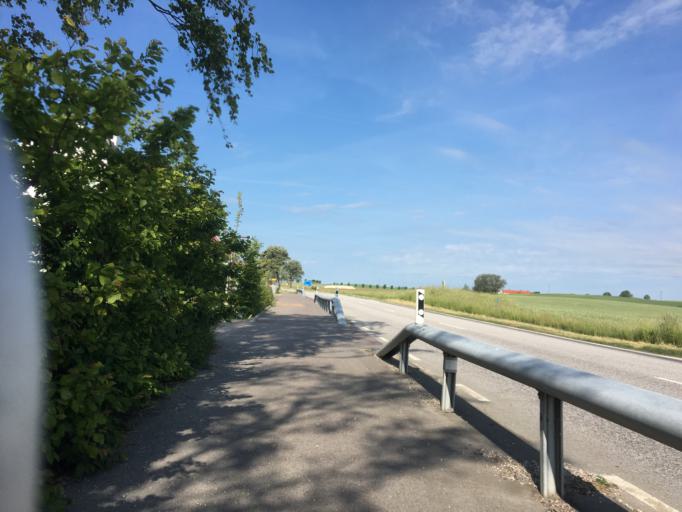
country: SE
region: Skane
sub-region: Skurups Kommun
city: Rydsgard
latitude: 55.4184
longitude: 13.6457
